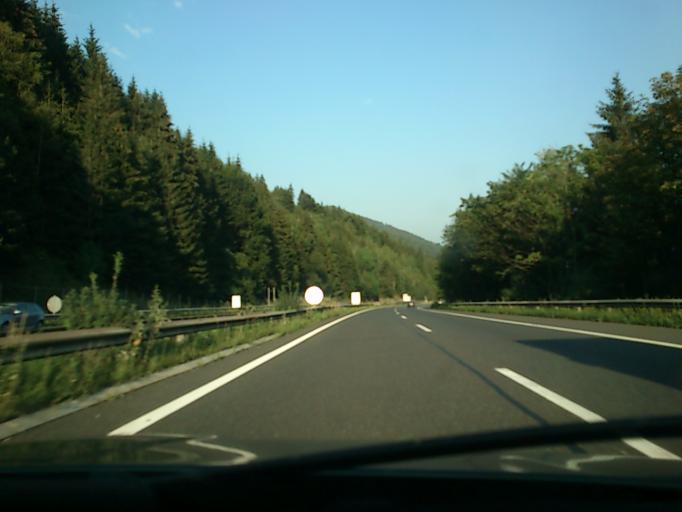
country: AT
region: Styria
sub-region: Politischer Bezirk Graz-Umgebung
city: Ubelbach
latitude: 47.2466
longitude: 15.1726
